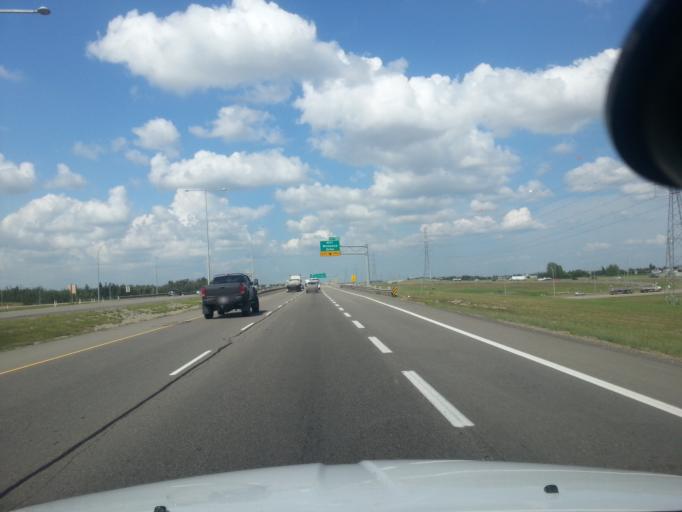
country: CA
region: Alberta
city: St. Albert
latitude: 53.5100
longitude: -113.6590
